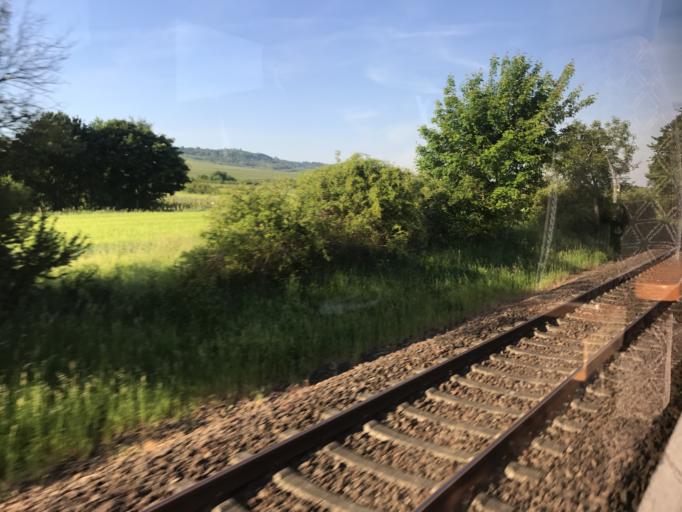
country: DE
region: Rheinland-Pfalz
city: Gau-Algesheim
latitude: 49.9543
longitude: 7.9954
